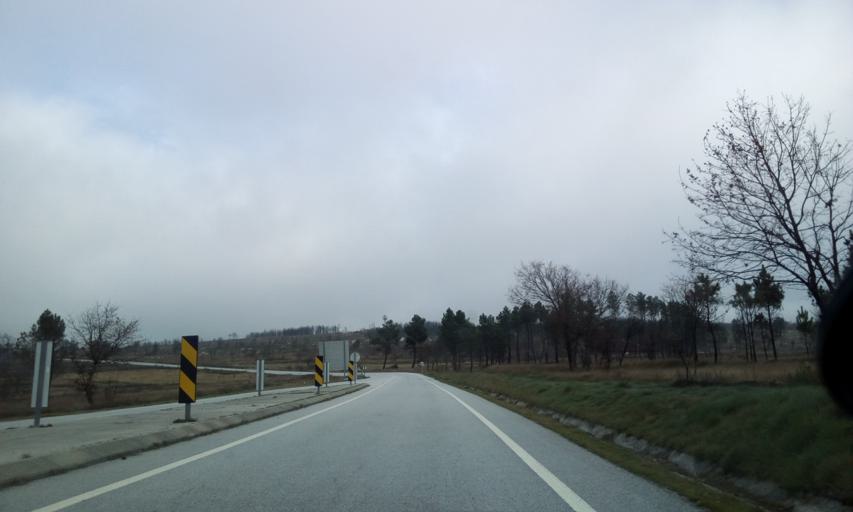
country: PT
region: Guarda
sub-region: Fornos de Algodres
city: Fornos de Algodres
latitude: 40.6963
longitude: -7.4736
